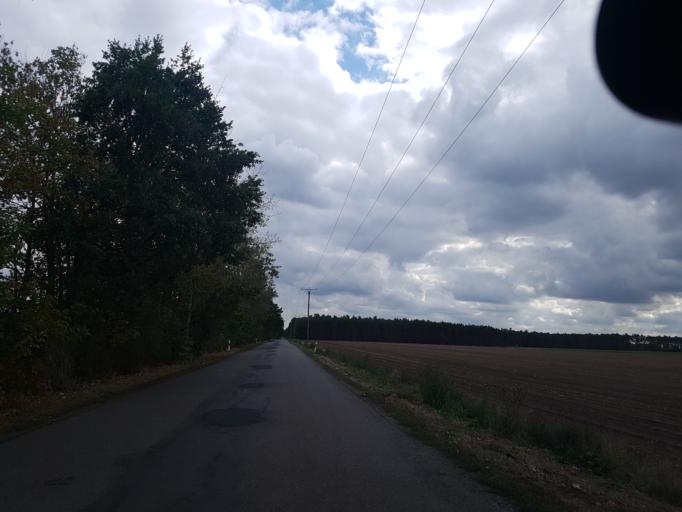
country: DE
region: Saxony-Anhalt
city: Rosslau
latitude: 51.9764
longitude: 12.2985
